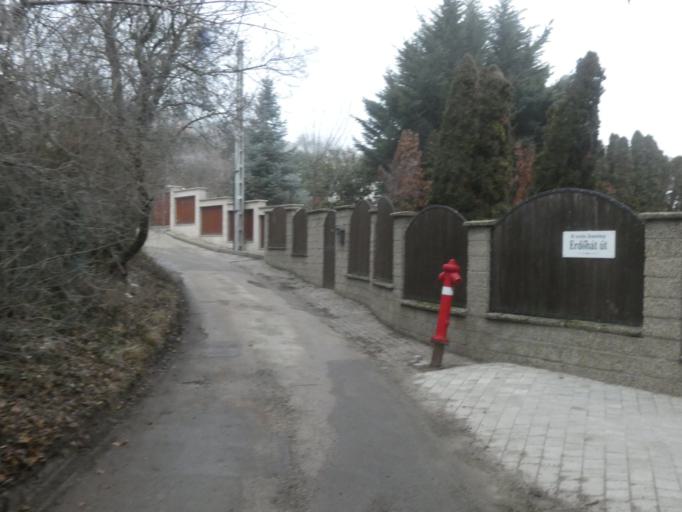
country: HU
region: Budapest
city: Budapest III. keruelet
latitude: 47.5396
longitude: 19.0163
